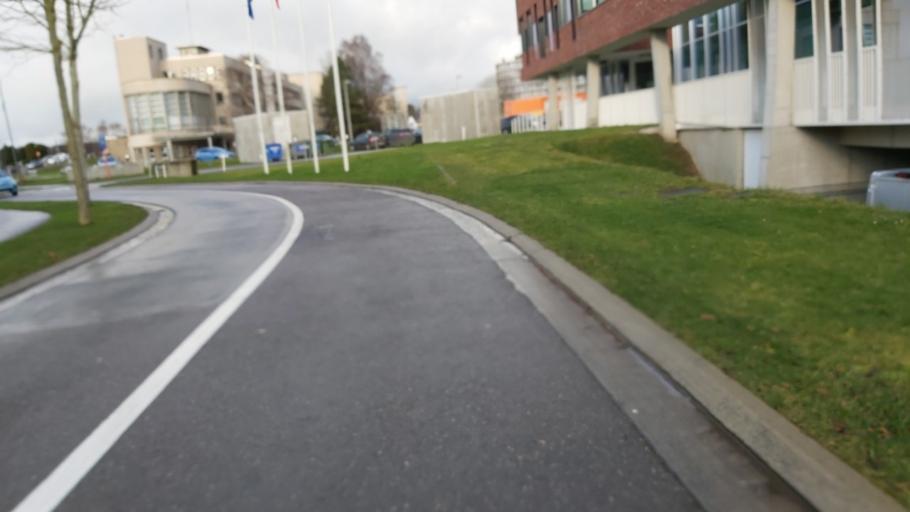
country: BE
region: Flanders
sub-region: Provincie Vlaams-Brabant
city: Tienen
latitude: 50.8132
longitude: 4.9408
